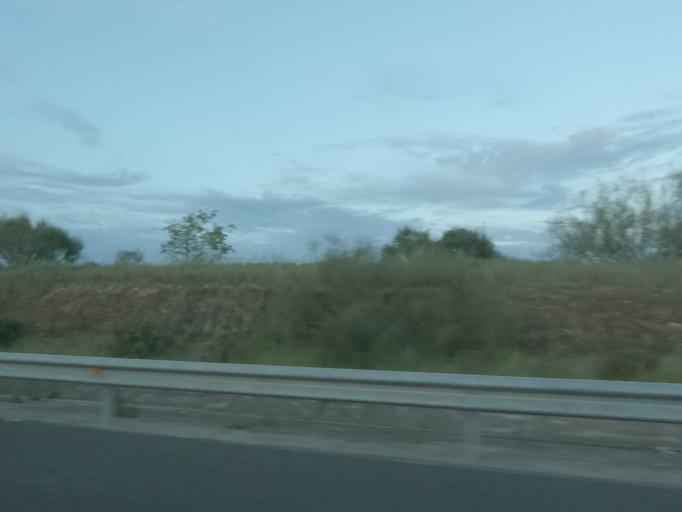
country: ES
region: Extremadura
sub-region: Provincia de Caceres
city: Caceres
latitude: 39.4138
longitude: -6.4020
